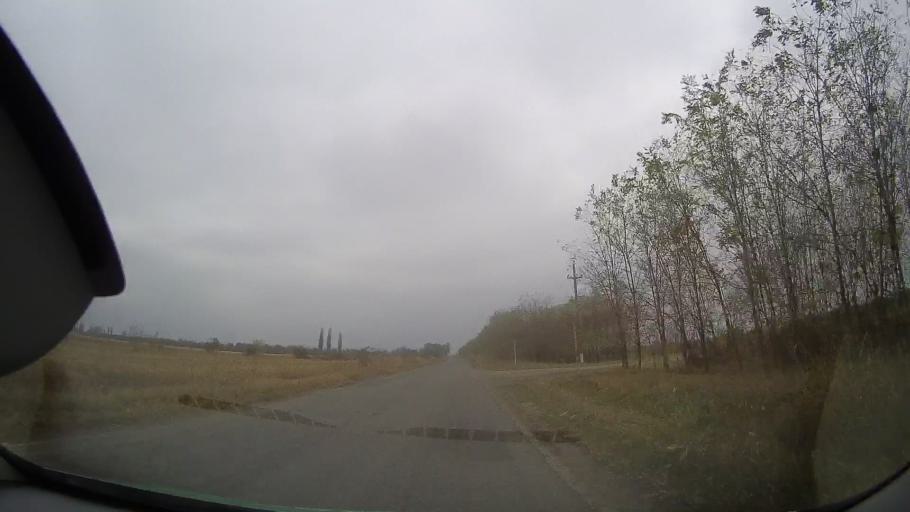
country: RO
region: Buzau
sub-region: Comuna Glodeanu-Silistea
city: Glodeanu-Silistea
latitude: 44.8133
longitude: 26.8499
